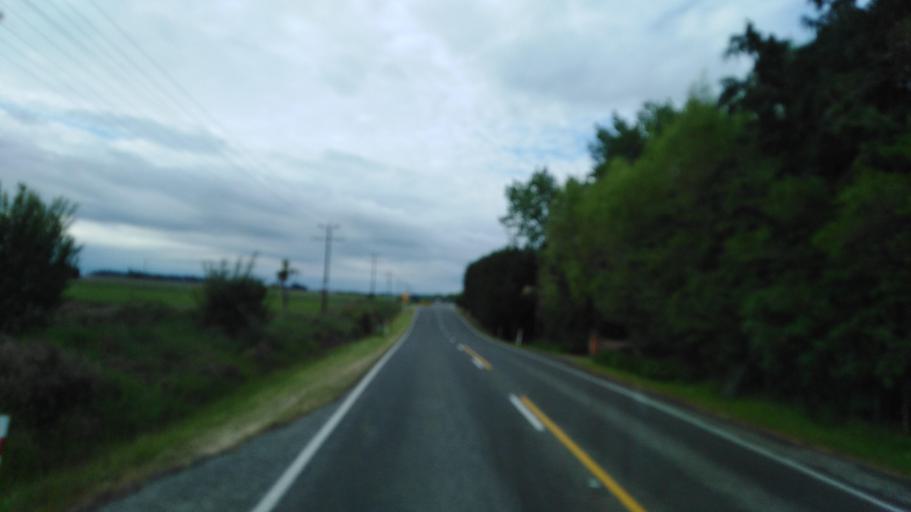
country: NZ
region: Manawatu-Wanganui
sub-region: Rangitikei District
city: Bulls
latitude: -40.1226
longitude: 175.3552
